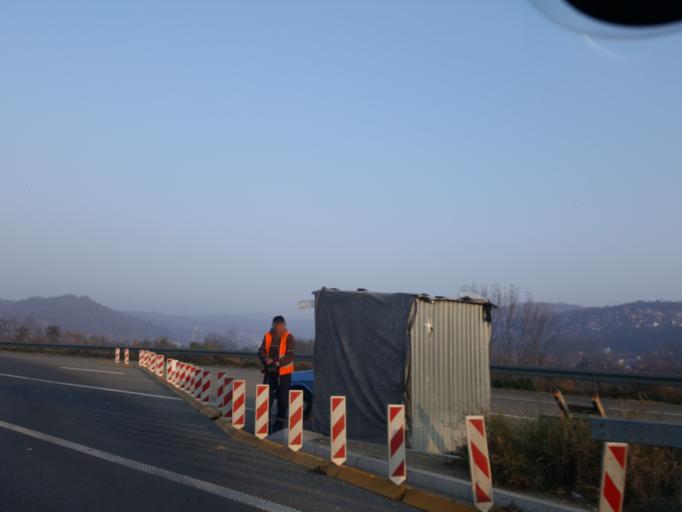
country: RS
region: Central Serbia
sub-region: Jablanicki Okrug
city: Vlasotince
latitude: 42.8812
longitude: 22.0770
